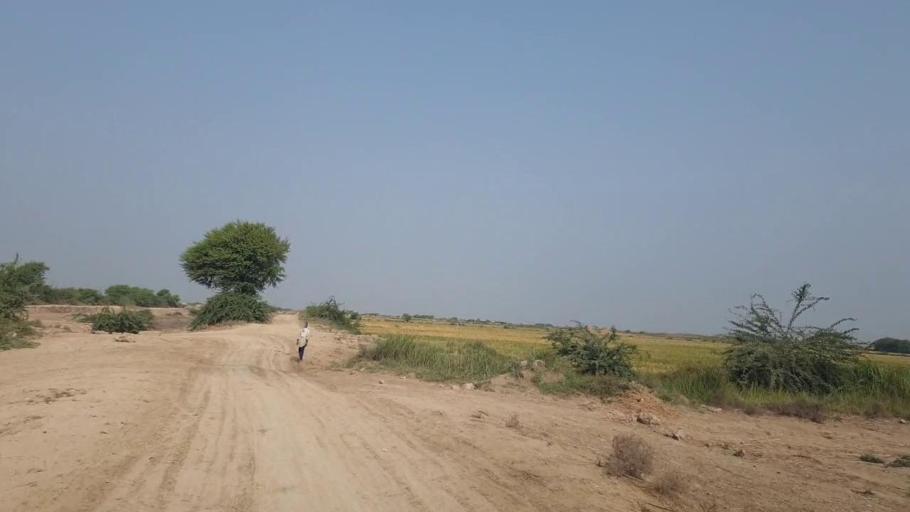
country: PK
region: Sindh
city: Badin
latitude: 24.7060
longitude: 68.7753
